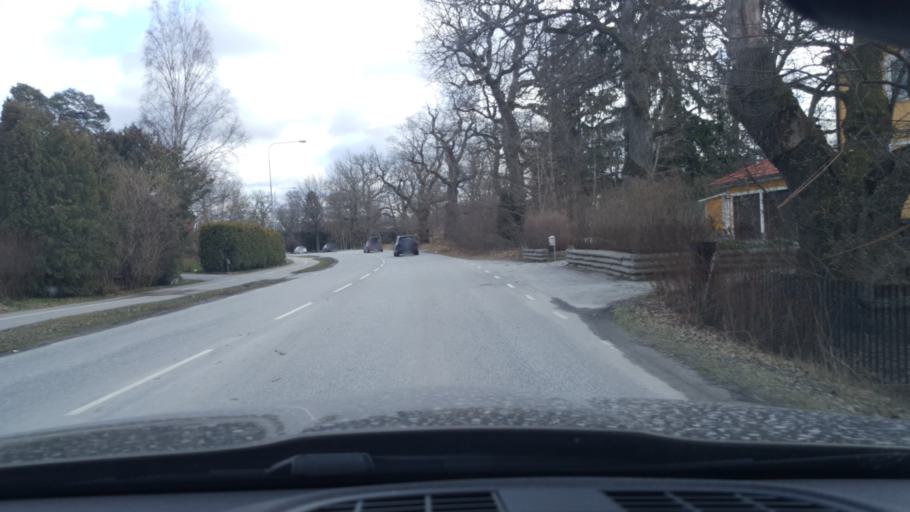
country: SE
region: Stockholm
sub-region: Osterakers Kommun
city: Akersberga
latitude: 59.4903
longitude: 18.2864
